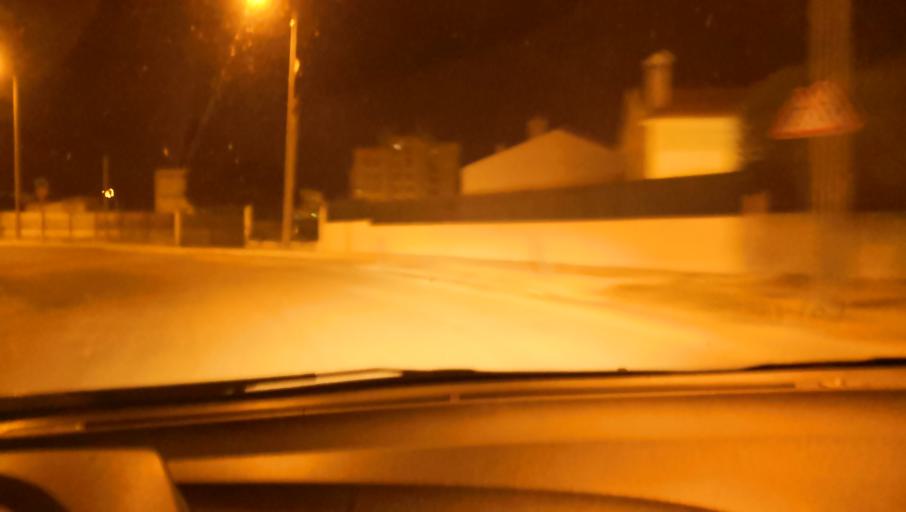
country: PT
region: Setubal
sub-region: Moita
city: Alhos Vedros
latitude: 38.6478
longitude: -9.0465
